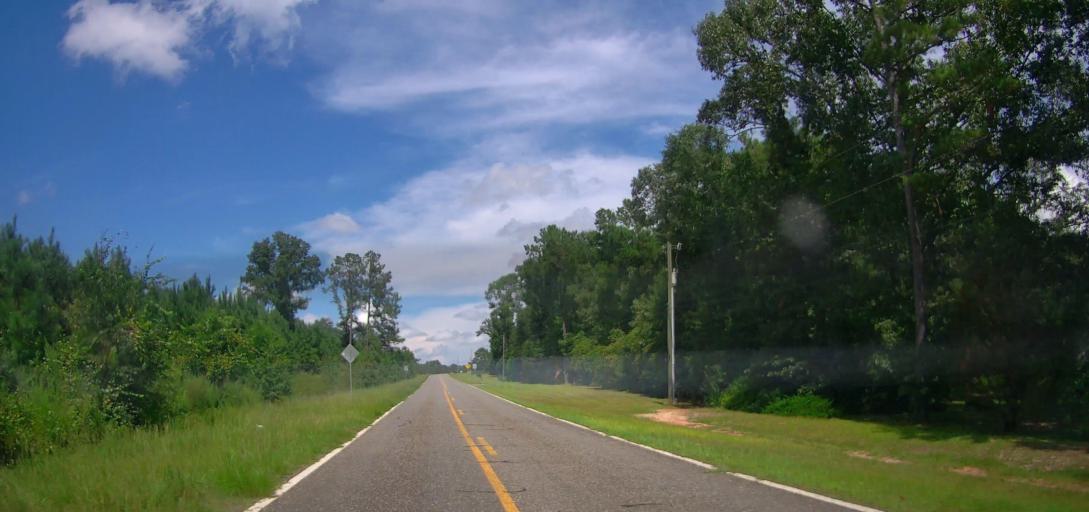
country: US
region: Georgia
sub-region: Peach County
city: Fort Valley
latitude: 32.5196
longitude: -83.8285
